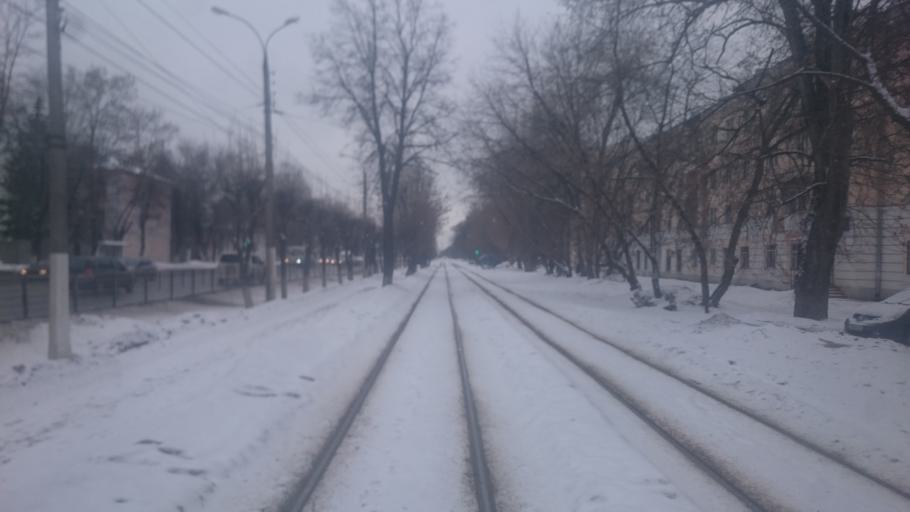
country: RU
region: Tverskaya
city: Tver
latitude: 56.8720
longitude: 35.8639
